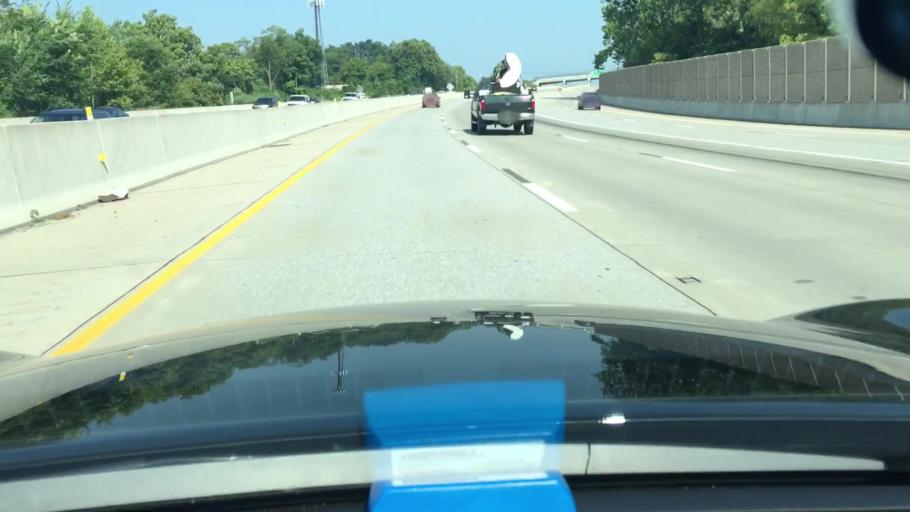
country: US
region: Pennsylvania
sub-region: Chester County
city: Malvern
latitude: 40.0517
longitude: -75.5409
